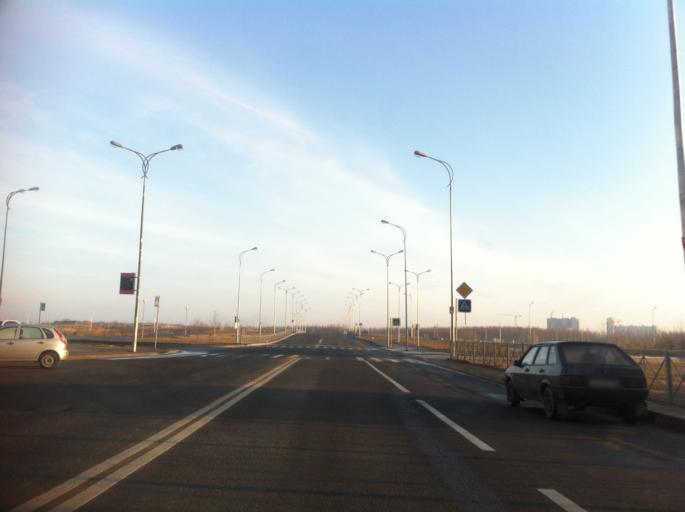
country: RU
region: St.-Petersburg
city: Sosnovaya Polyana
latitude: 59.8539
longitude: 30.1471
